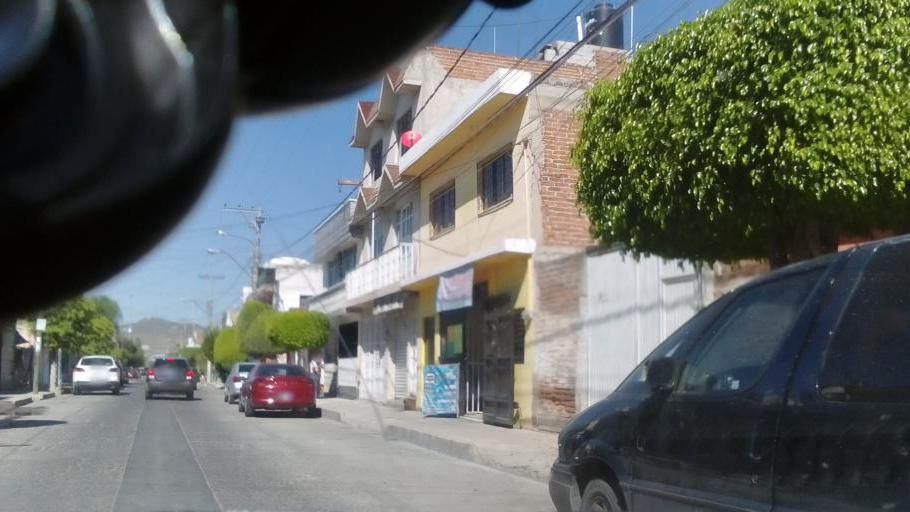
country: MX
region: Guanajuato
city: Leon
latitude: 21.1436
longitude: -101.6742
